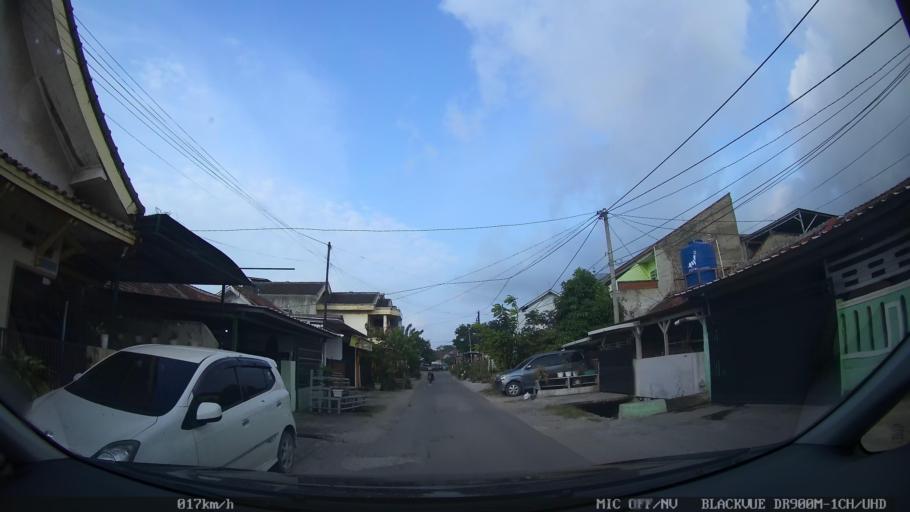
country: ID
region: Lampung
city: Kedaton
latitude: -5.4036
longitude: 105.3063
